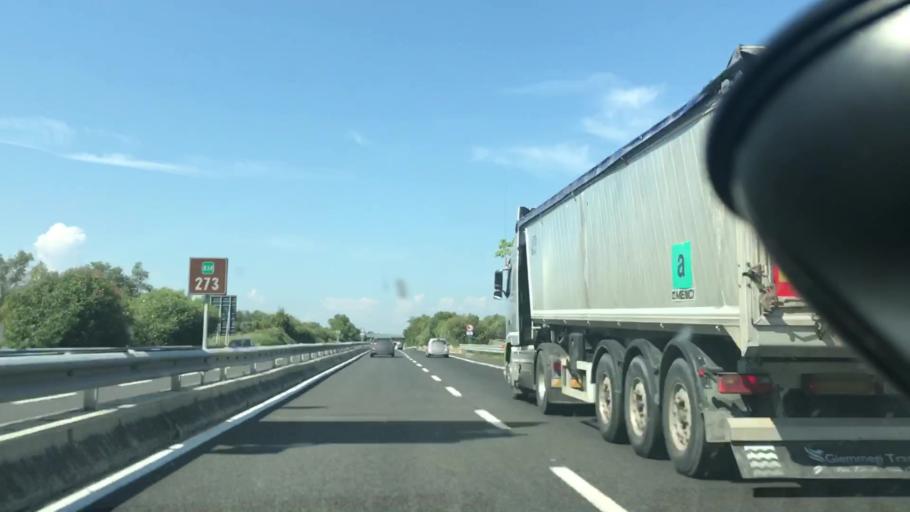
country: IT
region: Abruzzo
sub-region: Provincia di Chieti
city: Casalbordino-Miracoli
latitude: 42.1704
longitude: 14.6216
